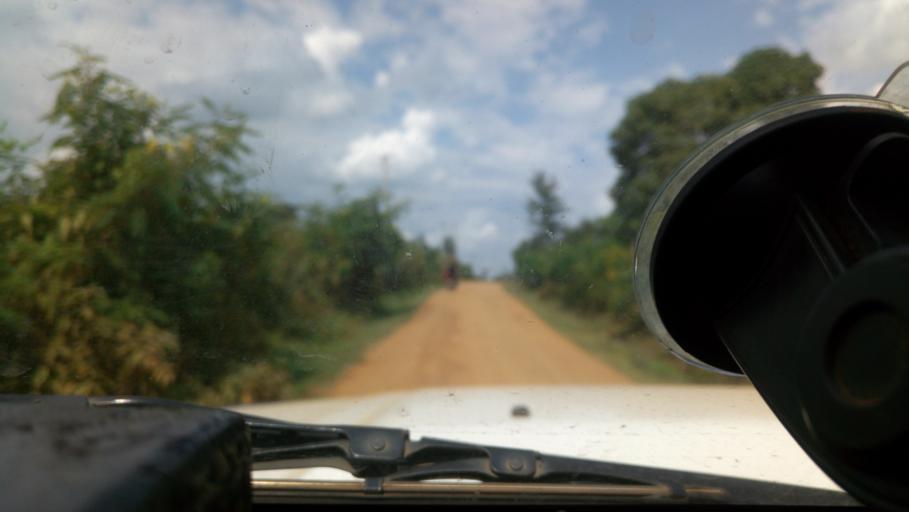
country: KE
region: Kericho
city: Sotik
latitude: -0.6529
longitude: 35.0885
